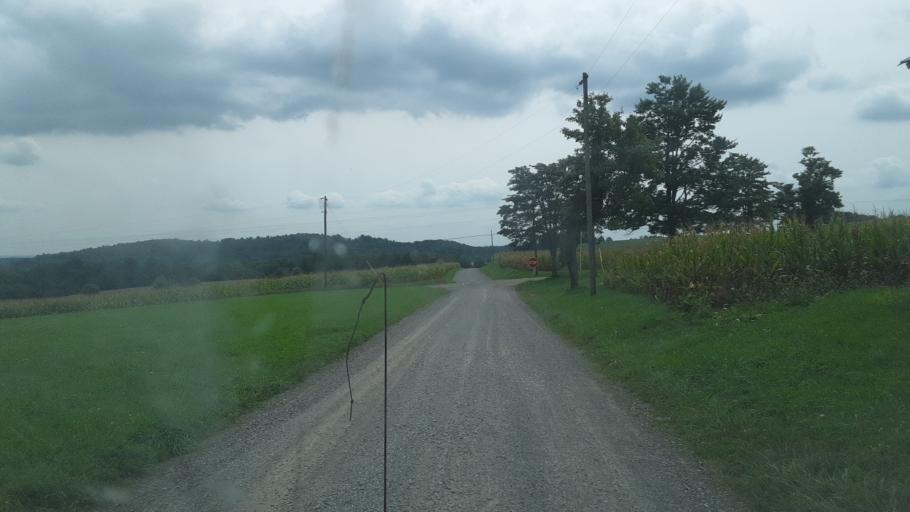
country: US
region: Pennsylvania
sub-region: Jefferson County
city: Punxsutawney
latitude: 40.9475
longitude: -79.1458
